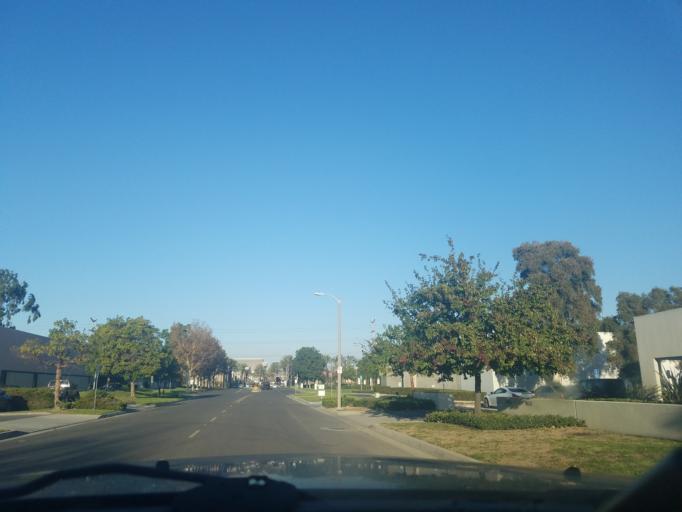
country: US
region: California
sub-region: Orange County
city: Irvine
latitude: 33.6942
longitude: -117.8306
